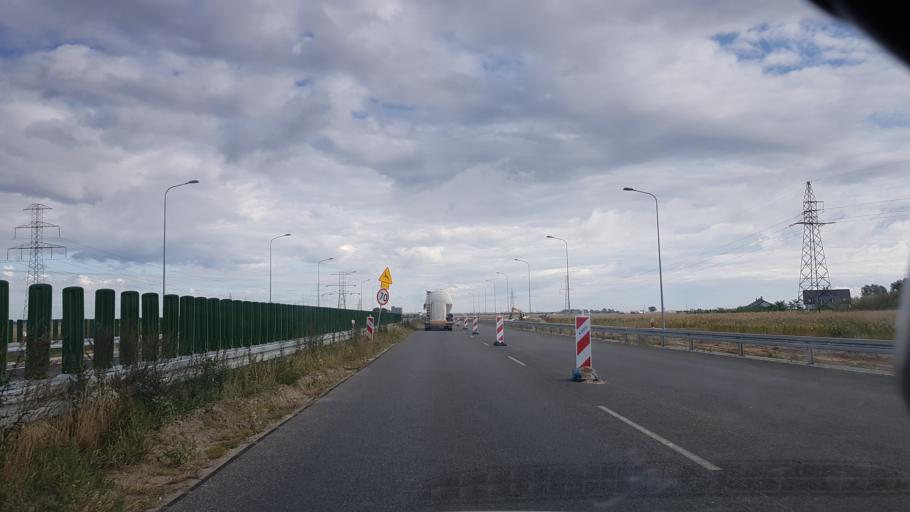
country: PL
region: Greater Poland Voivodeship
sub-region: Powiat poznanski
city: Steszew
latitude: 52.3349
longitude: 16.7356
